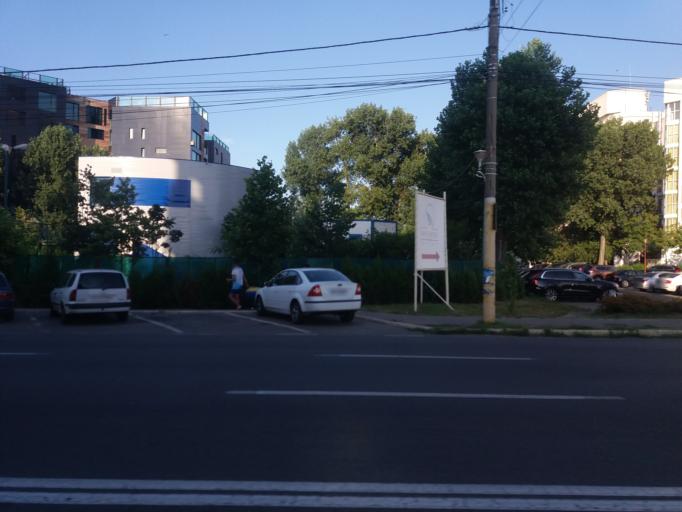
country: RO
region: Constanta
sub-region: Municipiul Constanta
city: Palazu Mare
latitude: 44.2627
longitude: 28.6183
